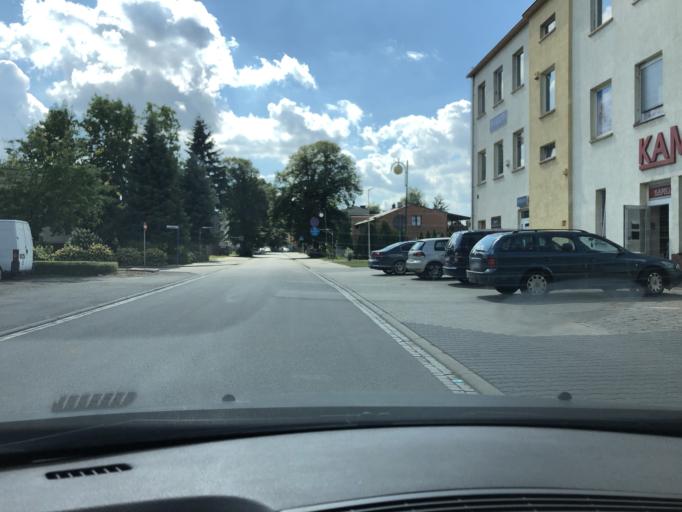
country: PL
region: Lodz Voivodeship
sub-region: Powiat wieruszowski
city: Wieruszow
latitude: 51.2971
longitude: 18.1596
